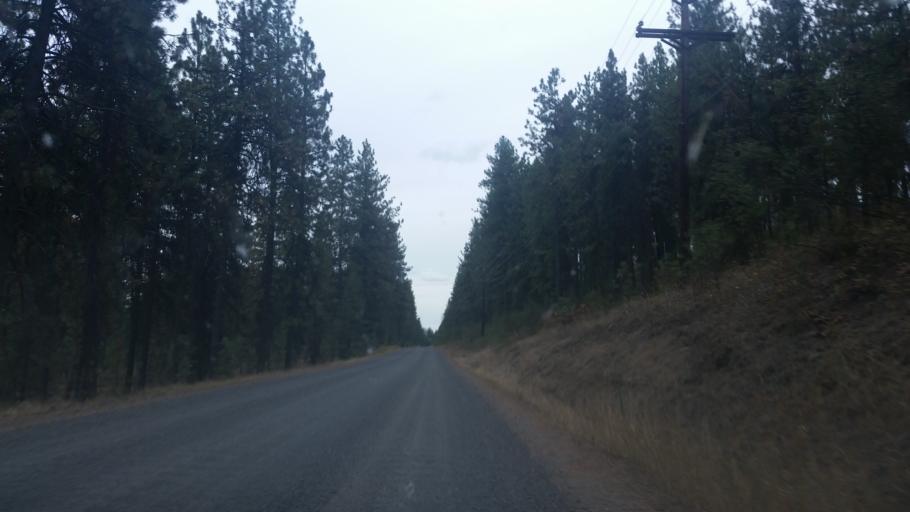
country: US
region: Washington
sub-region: Spokane County
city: Cheney
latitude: 47.5346
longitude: -117.5848
